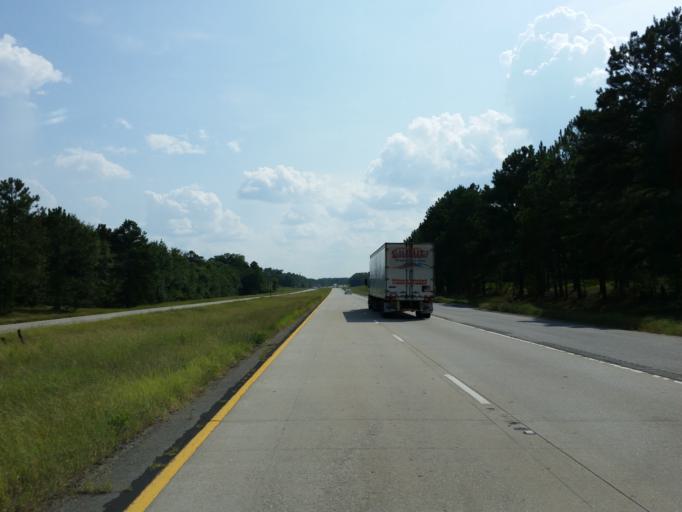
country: US
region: Georgia
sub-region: Crisp County
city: Cordele
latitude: 31.9309
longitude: -83.7534
